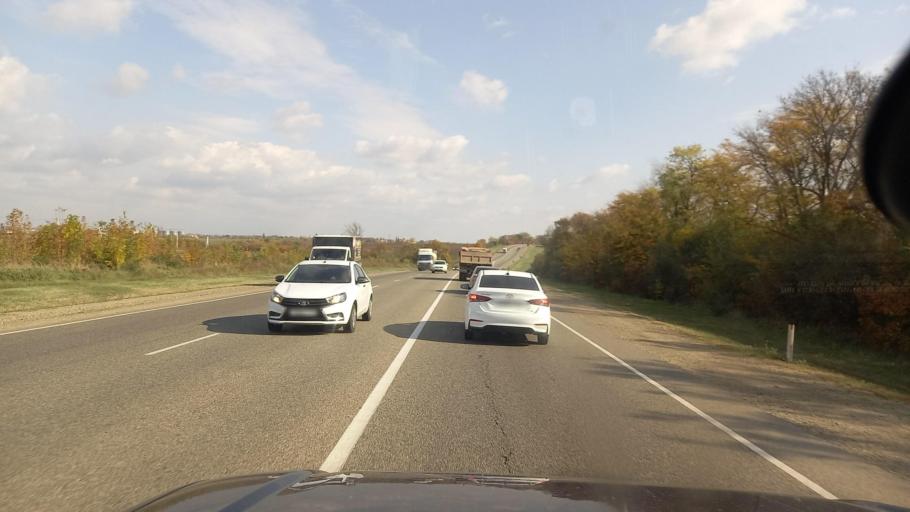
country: RU
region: Krasnodarskiy
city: Akhtyrskiy
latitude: 44.8520
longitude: 38.3194
